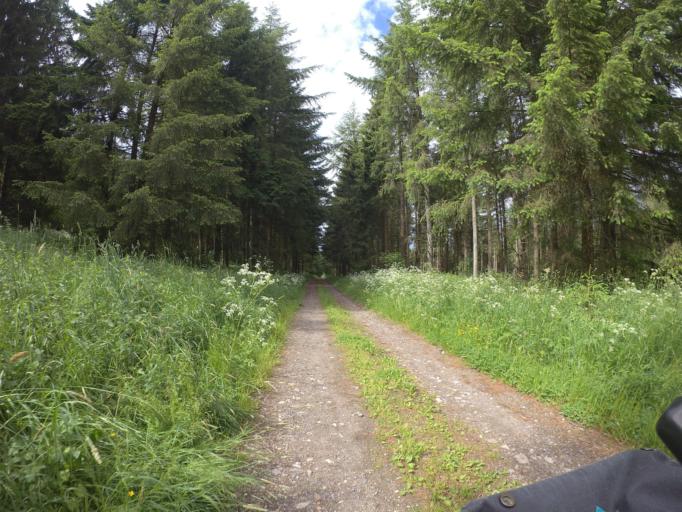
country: DE
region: Rheinland-Pfalz
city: Hinterweiler
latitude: 50.2347
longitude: 6.7665
